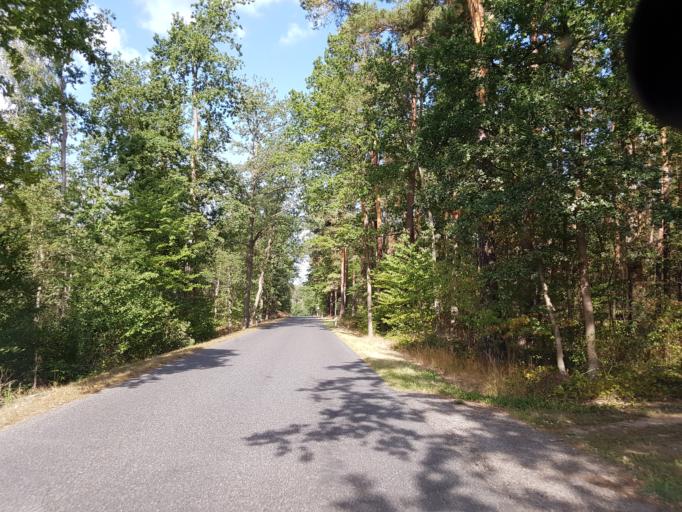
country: DE
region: Brandenburg
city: Sonnewalde
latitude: 51.7391
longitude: 13.6221
